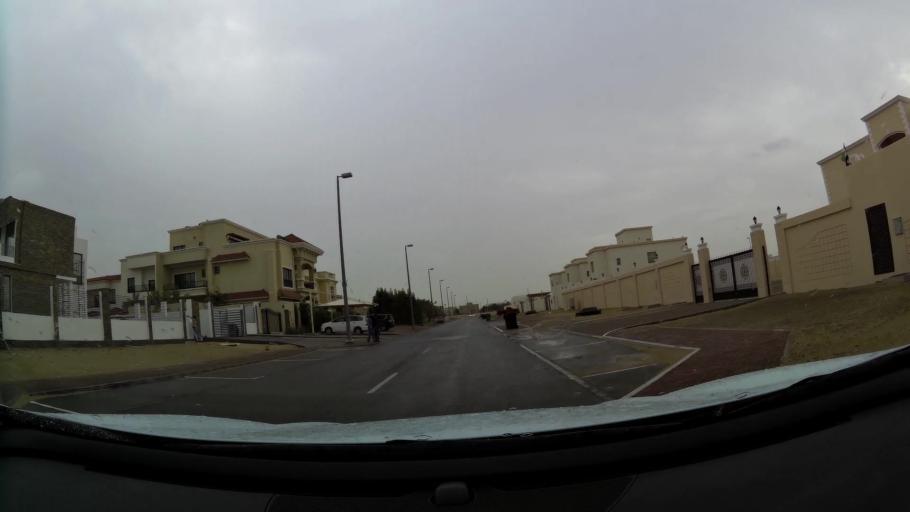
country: AE
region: Abu Dhabi
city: Abu Dhabi
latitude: 24.3649
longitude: 54.6377
